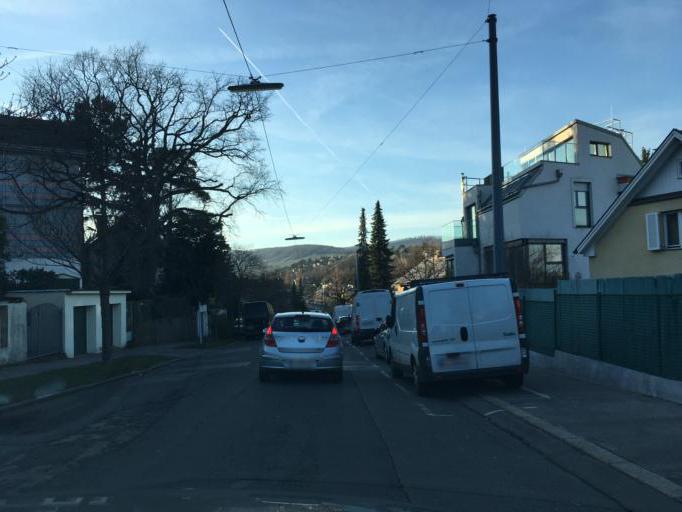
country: AT
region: Vienna
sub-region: Wien Stadt
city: Vienna
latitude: 48.2417
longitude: 16.3236
